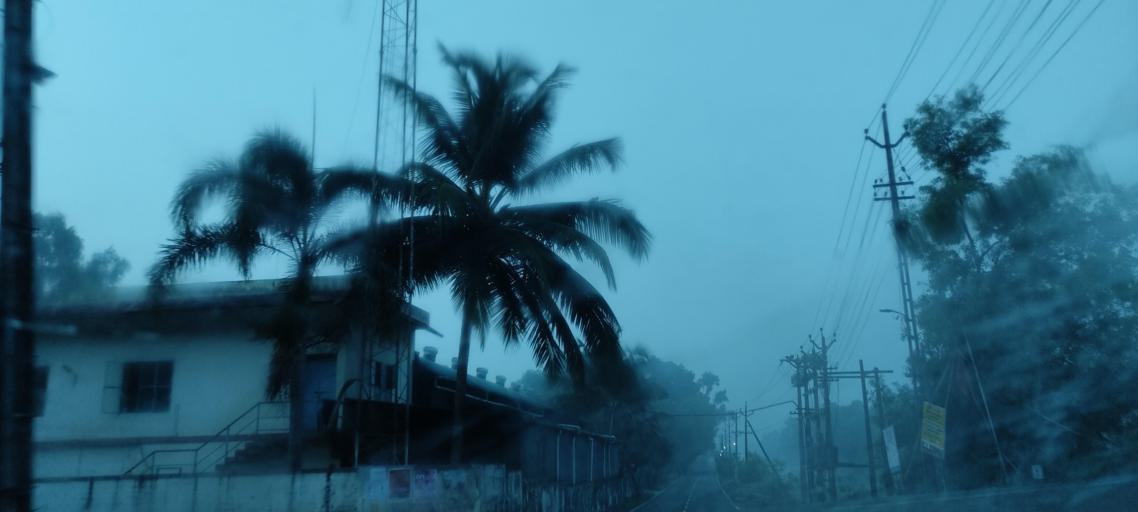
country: IN
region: Kerala
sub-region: Alappuzha
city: Shertallai
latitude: 9.5903
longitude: 76.3330
